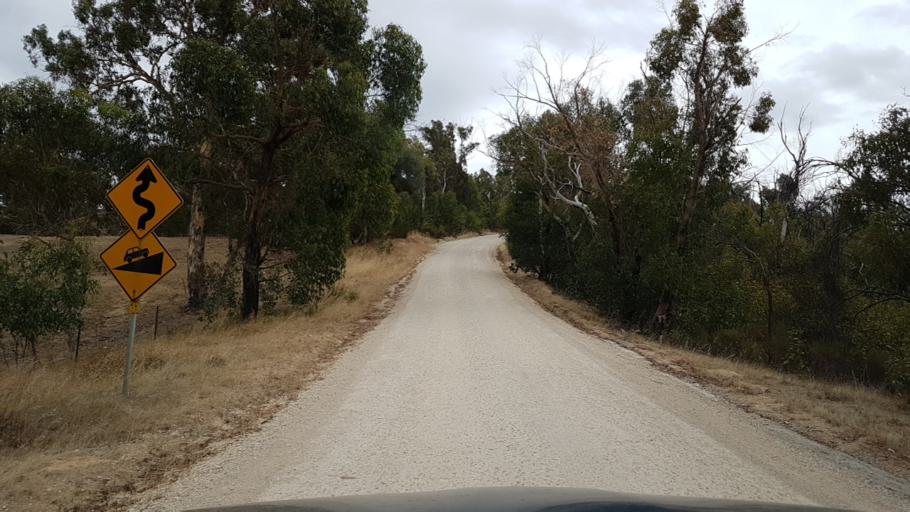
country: AU
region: South Australia
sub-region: Adelaide Hills
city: Gumeracha
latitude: -34.7912
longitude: 138.8138
